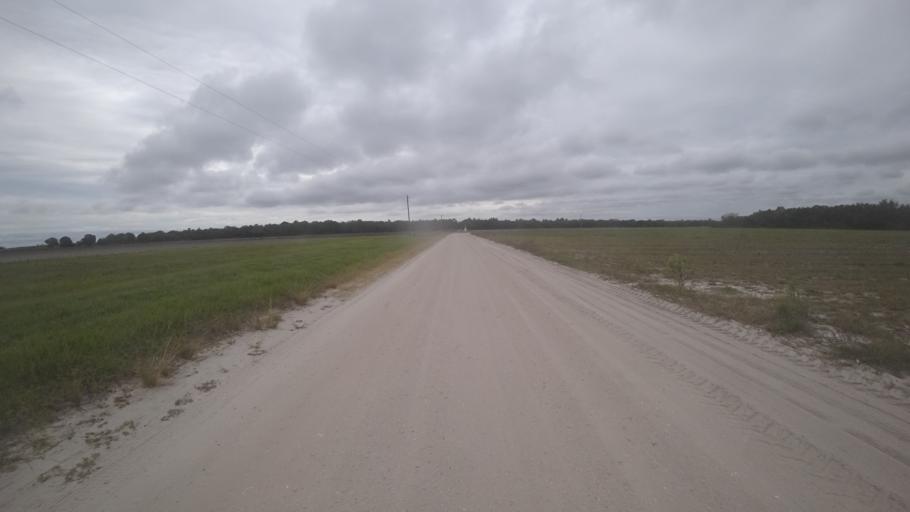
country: US
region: Florida
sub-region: Hillsborough County
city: Wimauma
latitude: 27.5870
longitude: -82.1226
